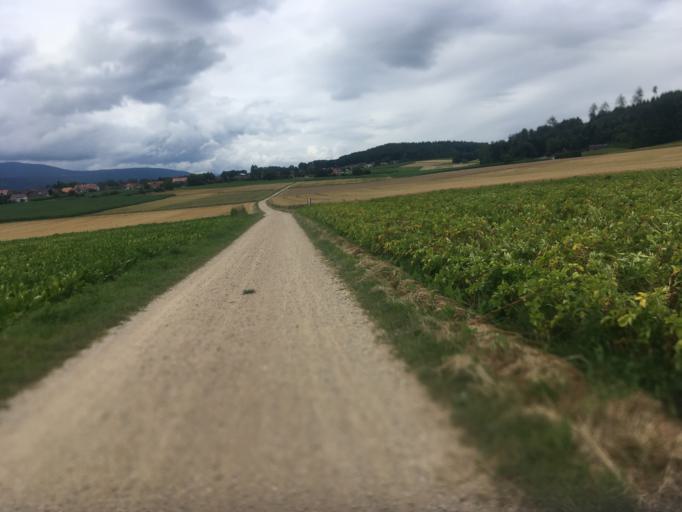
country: CH
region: Bern
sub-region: Seeland District
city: Ins
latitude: 47.0249
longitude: 7.1066
